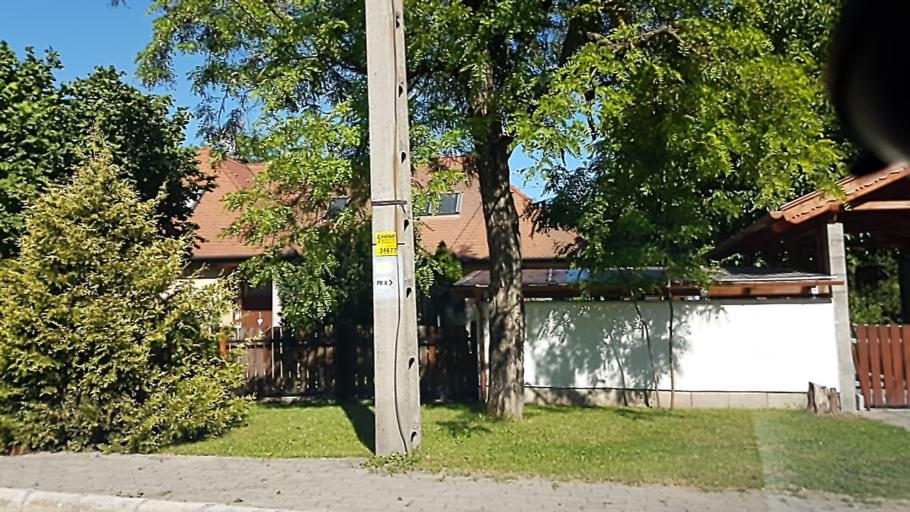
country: HU
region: Pest
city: Pilisszentivan
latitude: 47.6060
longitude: 18.9016
